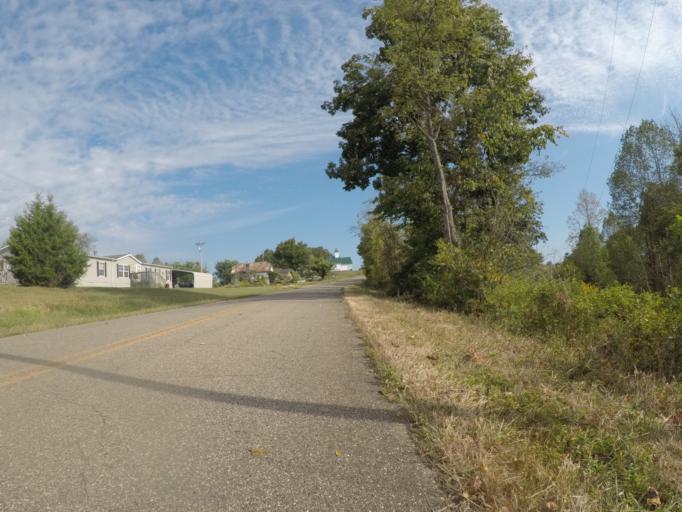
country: US
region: West Virginia
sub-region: Cabell County
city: Lesage
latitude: 38.5654
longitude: -82.4276
